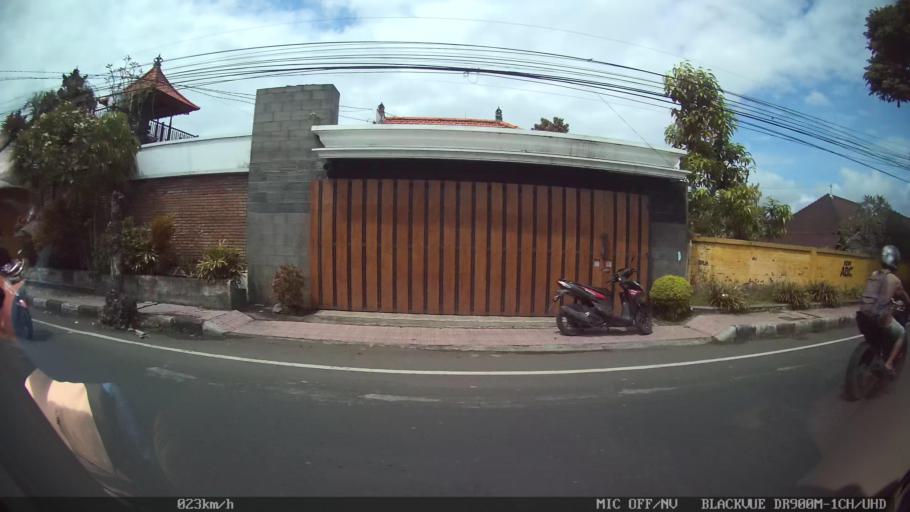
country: ID
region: Bali
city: Banjar Pesalakan
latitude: -8.5347
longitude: 115.3153
